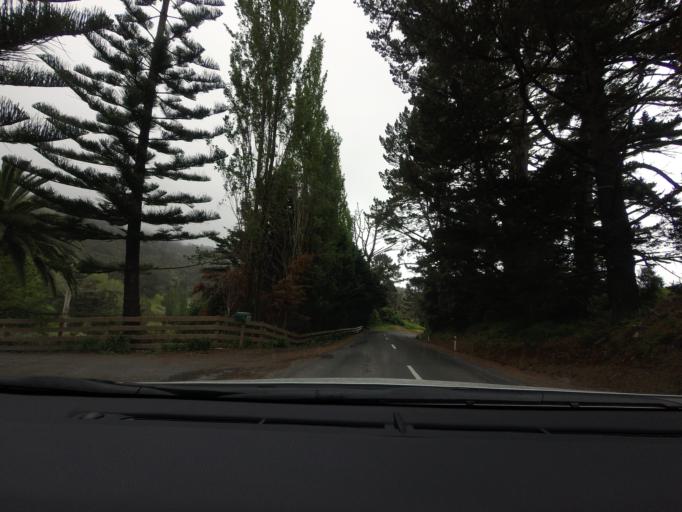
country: NZ
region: Auckland
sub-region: Auckland
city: Warkworth
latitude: -36.2809
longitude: 174.7913
